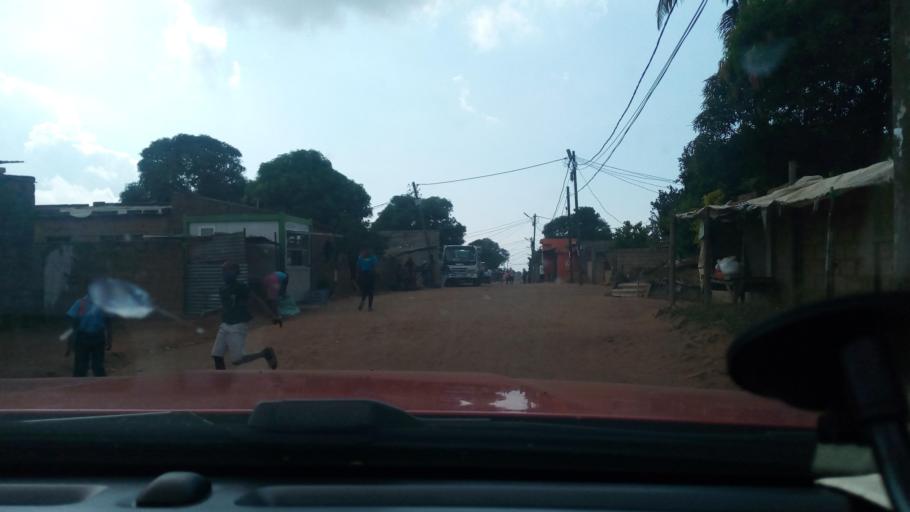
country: MZ
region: Maputo City
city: Maputo
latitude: -25.9202
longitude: 32.5991
